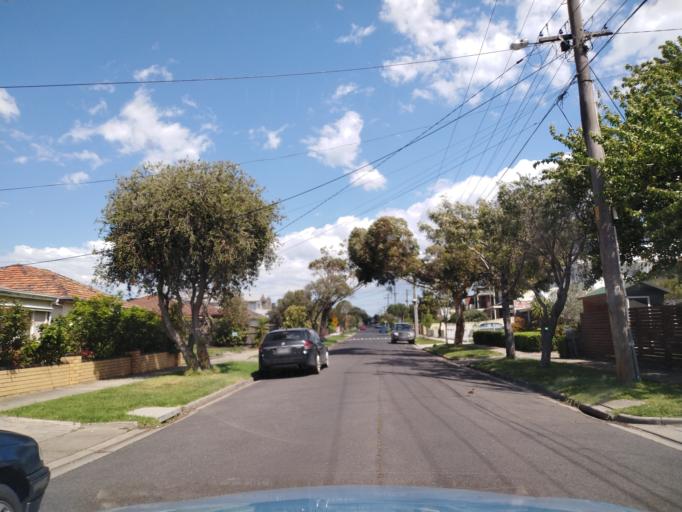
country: AU
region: Victoria
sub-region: Hobsons Bay
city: South Kingsville
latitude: -37.8302
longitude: 144.8738
